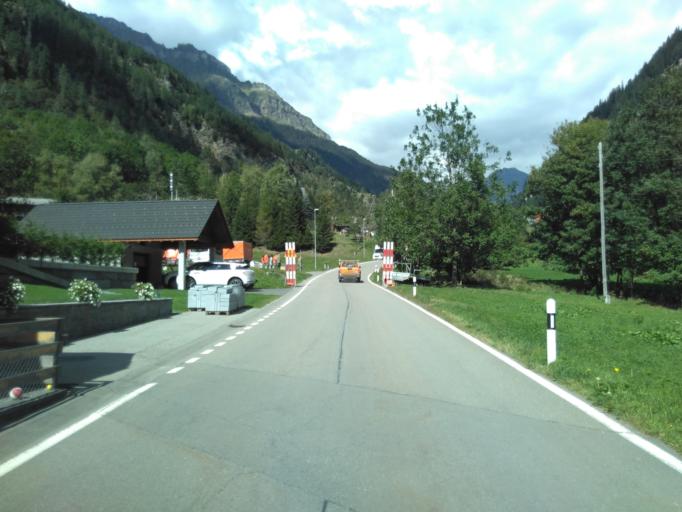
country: CH
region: Grisons
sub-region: Moesa District
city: Cauco
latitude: 46.3688
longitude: 9.1261
